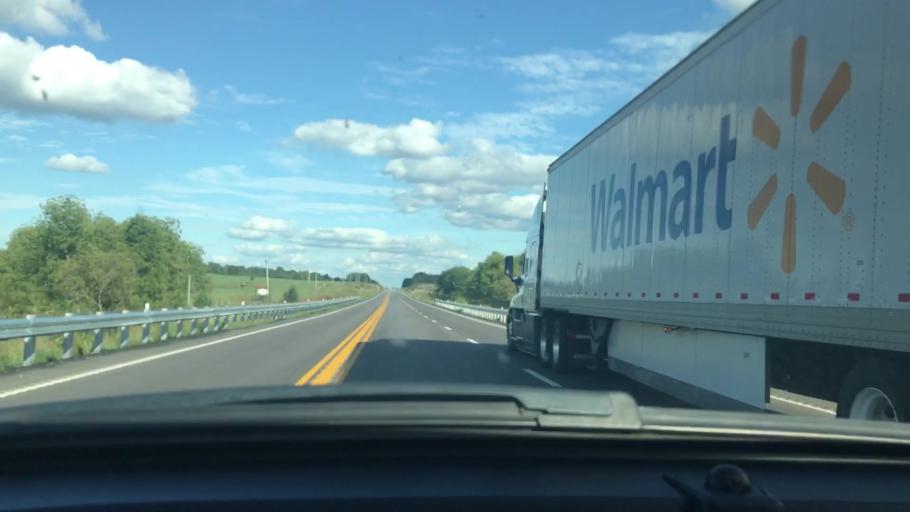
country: US
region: Missouri
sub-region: Oregon County
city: Thayer
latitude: 36.5864
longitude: -91.6263
